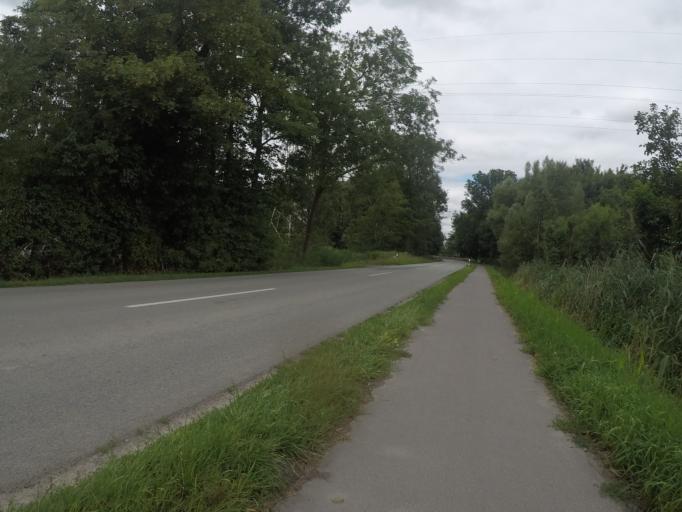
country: DE
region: Lower Saxony
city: Himmelpforten
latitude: 53.6518
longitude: 9.2976
